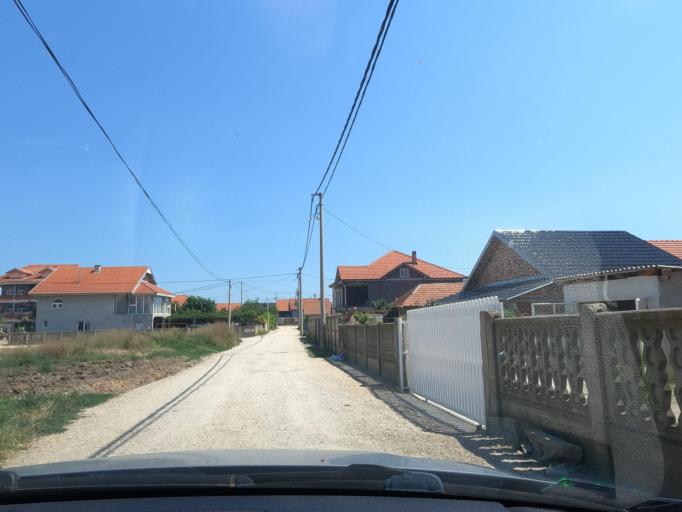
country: RS
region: Central Serbia
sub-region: Branicevski Okrug
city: Pozarevac
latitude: 44.7038
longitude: 21.1666
